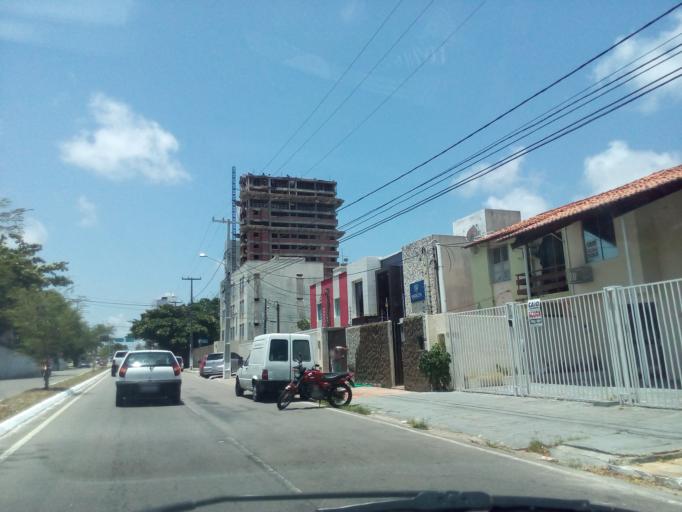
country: BR
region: Rio Grande do Norte
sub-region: Natal
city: Natal
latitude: -5.8266
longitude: -35.2080
